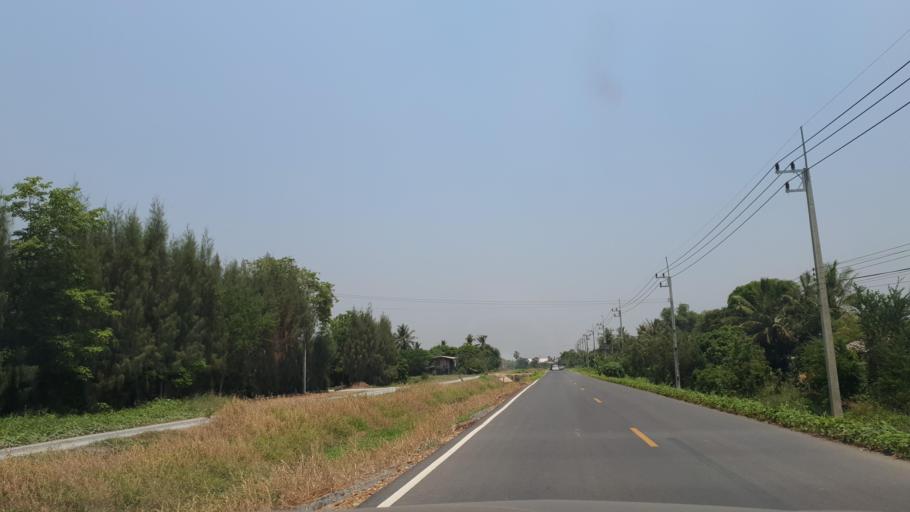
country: TH
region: Suphan Buri
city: Si Prachan
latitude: 14.5945
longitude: 100.1035
